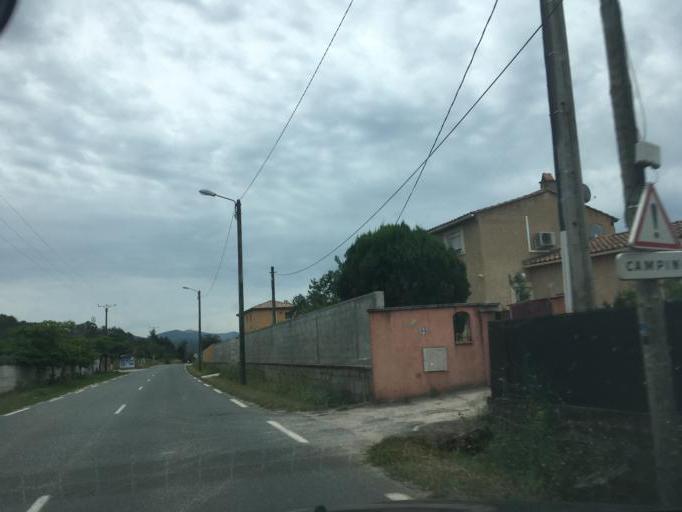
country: FR
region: Provence-Alpes-Cote d'Azur
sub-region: Departement du Var
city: Pierrefeu-du-Var
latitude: 43.2333
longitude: 6.1602
